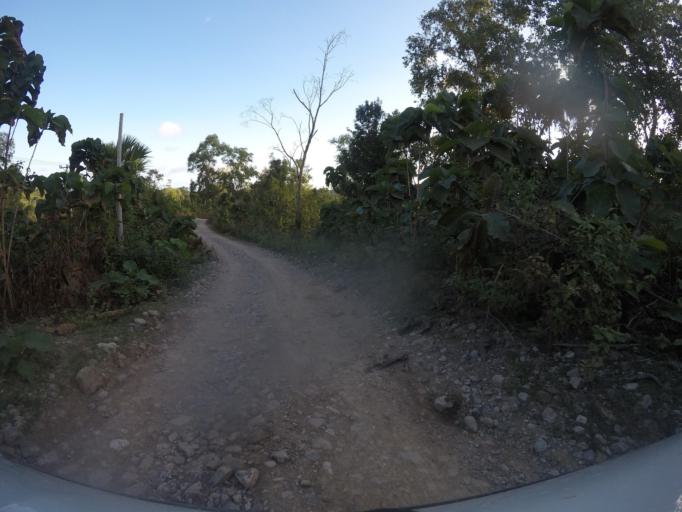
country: TL
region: Baucau
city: Venilale
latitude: -8.7168
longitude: 126.7126
